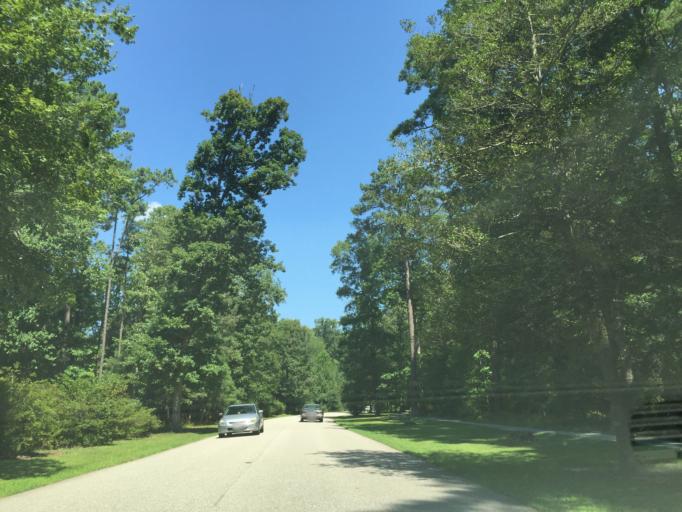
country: US
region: Virginia
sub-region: City of Newport News
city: Newport News
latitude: 37.0507
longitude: -76.4891
